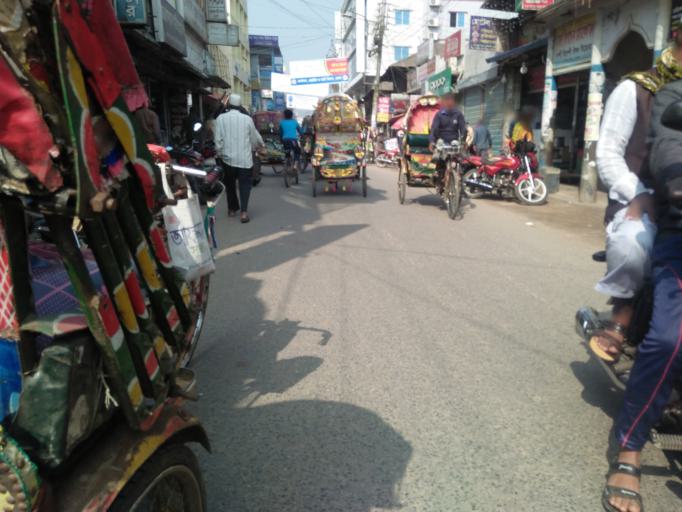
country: BD
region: Barisal
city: Bhola
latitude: 22.6844
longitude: 90.6450
